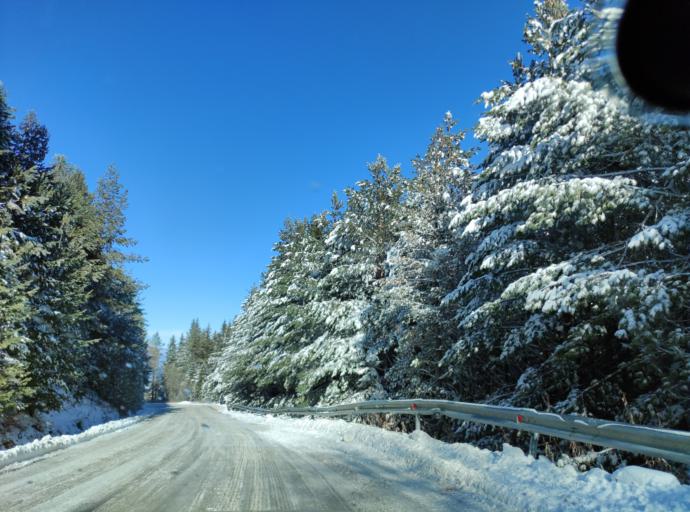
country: BG
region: Sofia-Capital
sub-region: Stolichna Obshtina
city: Sofia
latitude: 42.5905
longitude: 23.2965
